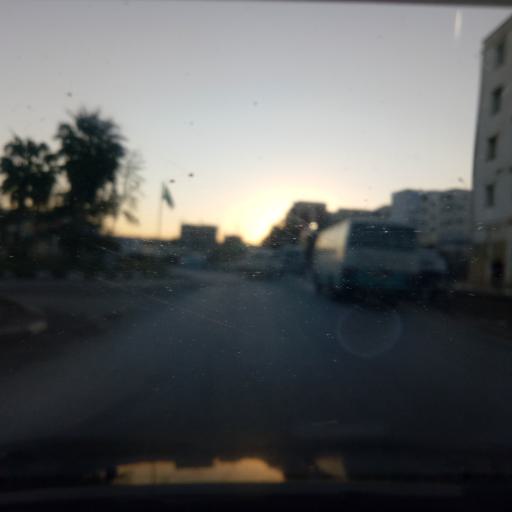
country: DZ
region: Tipaza
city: Bou Ismail
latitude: 36.6407
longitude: 2.7070
